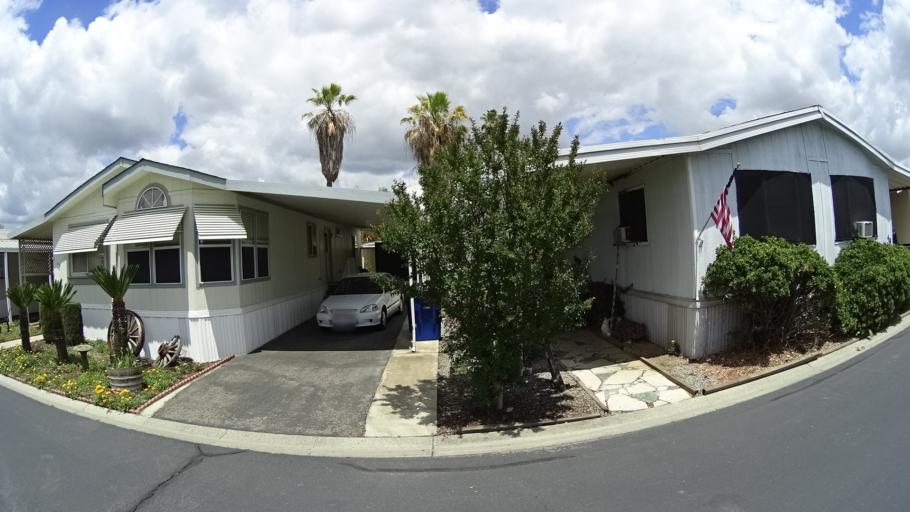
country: US
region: California
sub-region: Kings County
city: Hanford
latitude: 36.3460
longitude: -119.6316
